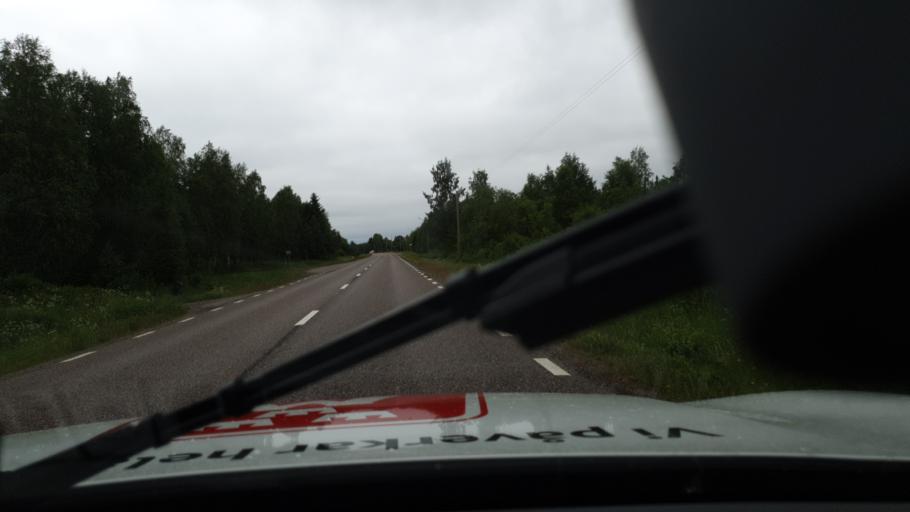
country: FI
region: Lapland
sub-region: Torniolaakso
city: Pello
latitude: 66.9377
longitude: 23.8511
